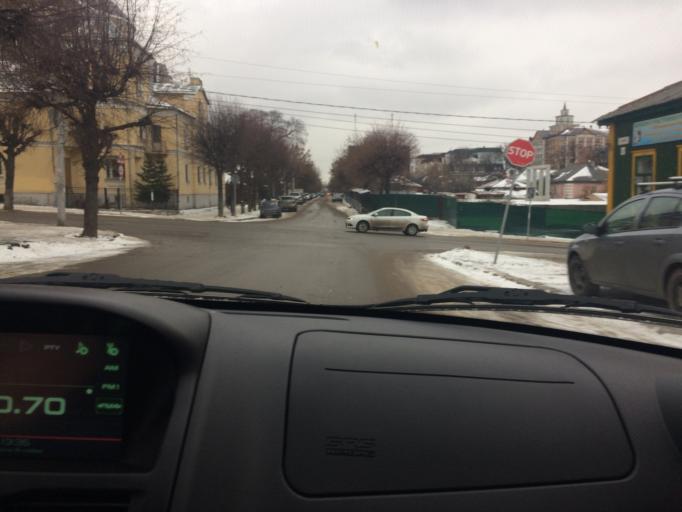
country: RU
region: Rjazan
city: Ryazan'
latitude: 54.6271
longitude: 39.7589
